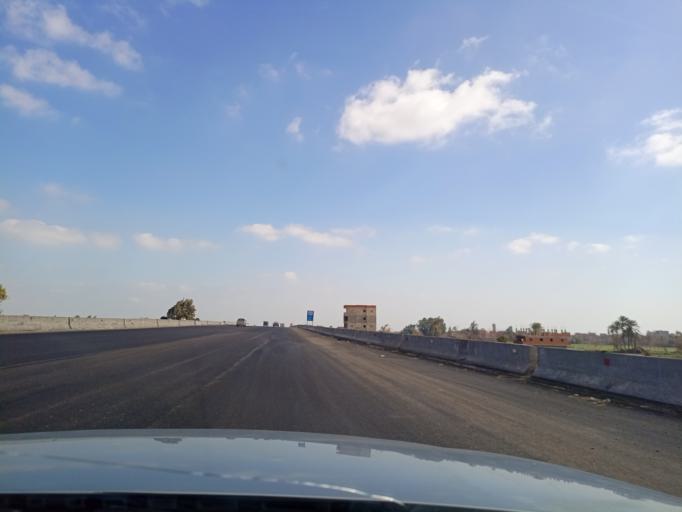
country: EG
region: Muhafazat al Minufiyah
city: Al Bajur
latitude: 30.4066
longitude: 31.0448
